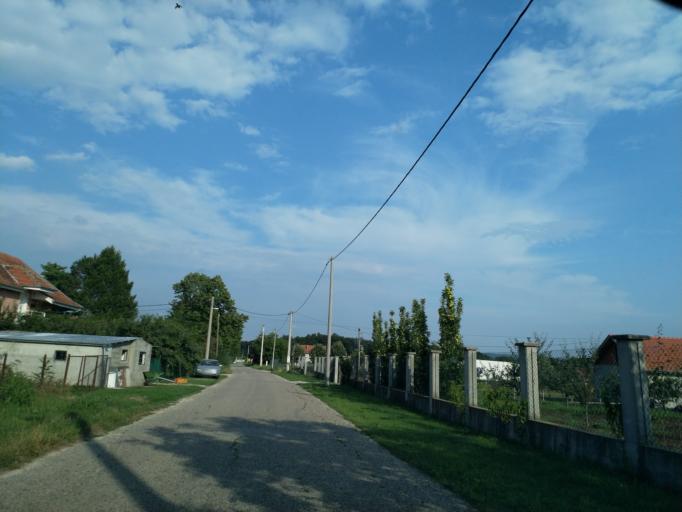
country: RS
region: Central Serbia
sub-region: Pomoravski Okrug
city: Jagodina
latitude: 43.9857
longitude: 21.2160
